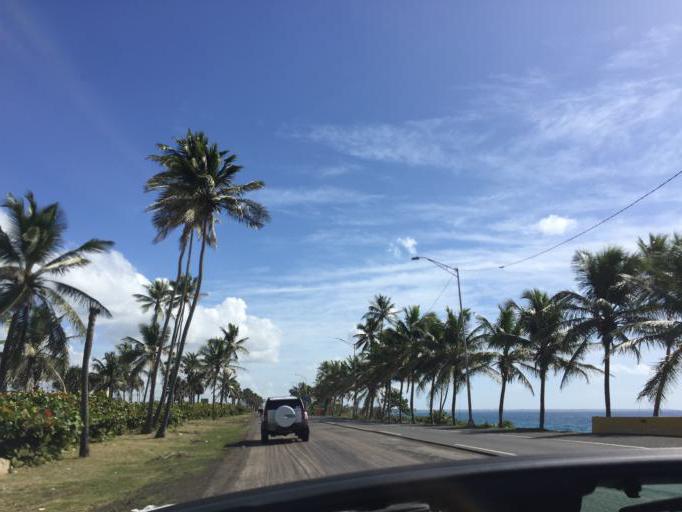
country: DO
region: Santo Domingo
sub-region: Santo Domingo
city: Santo Domingo Este
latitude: 18.4636
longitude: -69.7536
